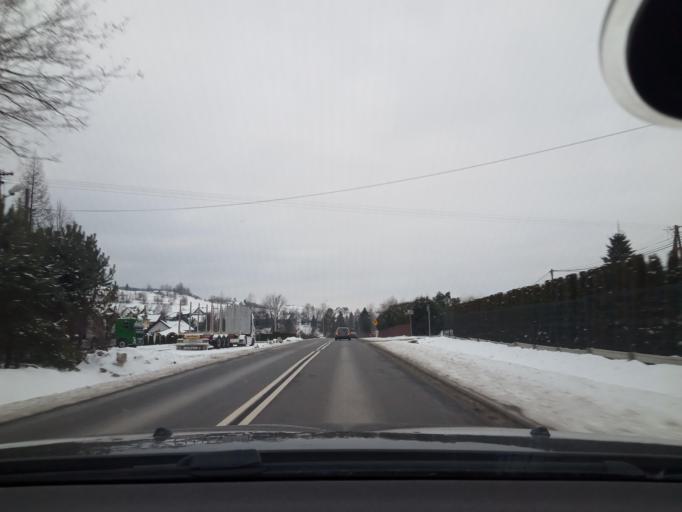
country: PL
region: Lesser Poland Voivodeship
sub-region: Powiat limanowski
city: Lubomierz
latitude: 49.6082
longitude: 20.2002
